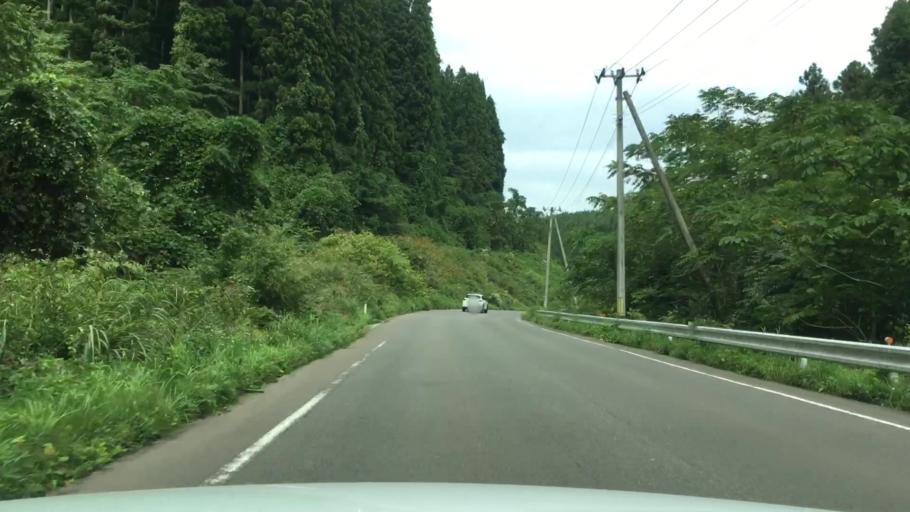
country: JP
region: Aomori
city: Shimokizukuri
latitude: 40.7396
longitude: 140.2451
